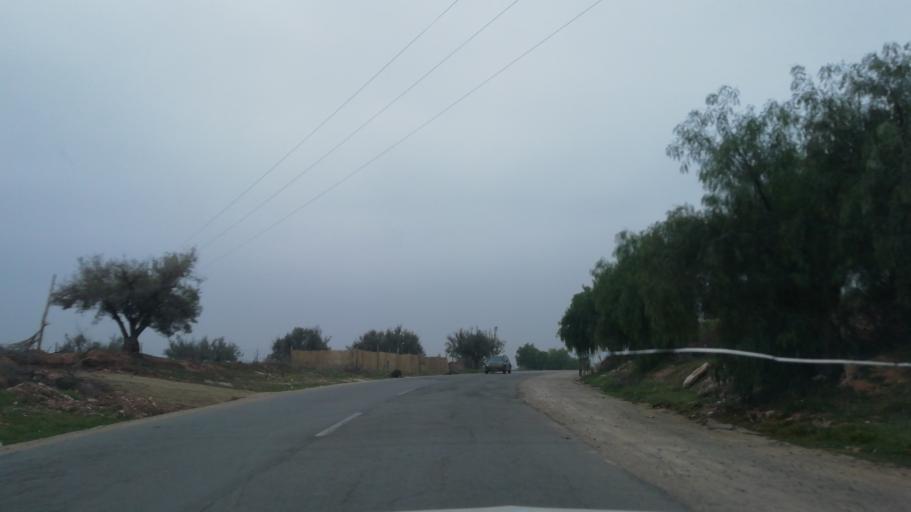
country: DZ
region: Mascara
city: Mascara
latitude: 35.3972
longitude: 0.1654
